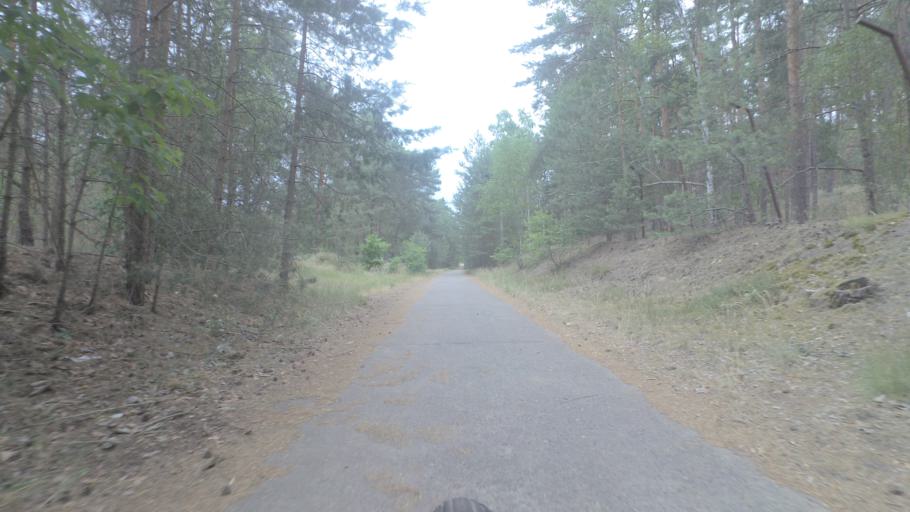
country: DE
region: Brandenburg
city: Ludwigsfelde
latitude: 52.3220
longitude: 13.2531
